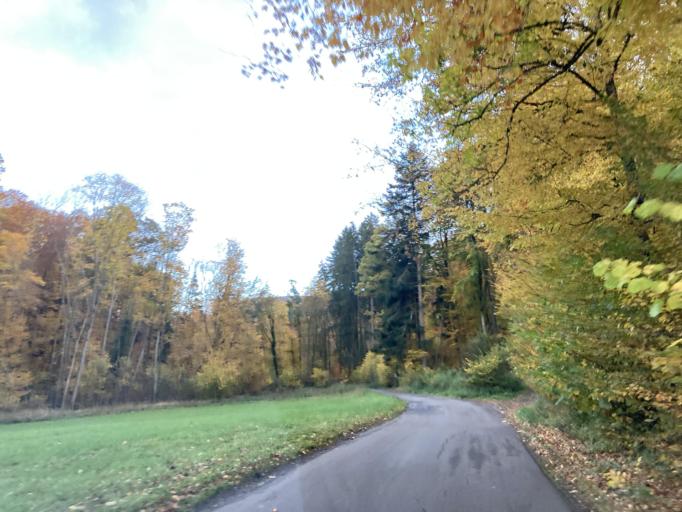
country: DE
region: Baden-Wuerttemberg
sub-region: Tuebingen Region
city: Gomaringen
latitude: 48.4369
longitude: 9.1095
